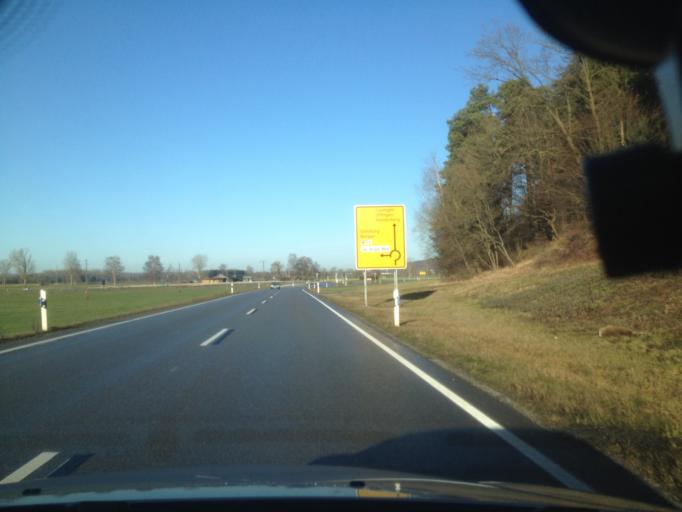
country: DE
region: Bavaria
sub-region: Swabia
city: Haldenwang
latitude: 48.4419
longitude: 10.4288
